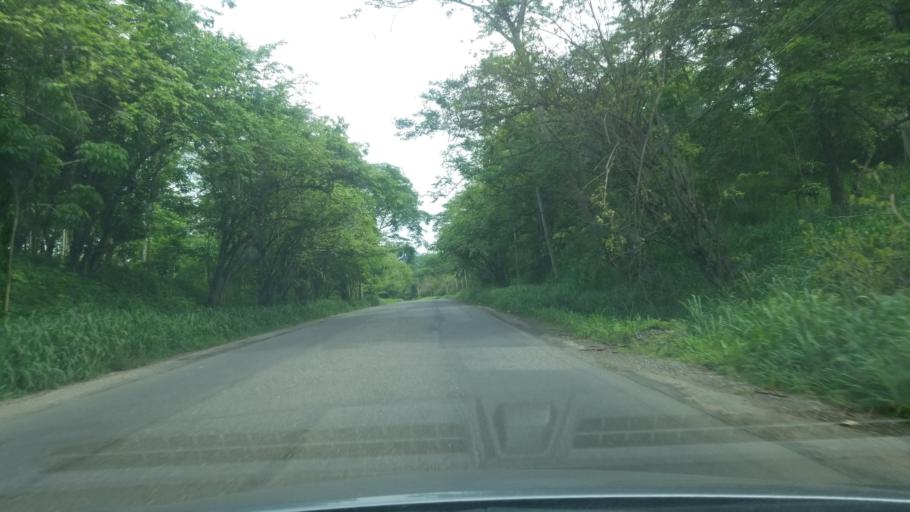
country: HN
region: Santa Barbara
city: Camalote
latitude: 15.3237
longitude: -88.3156
